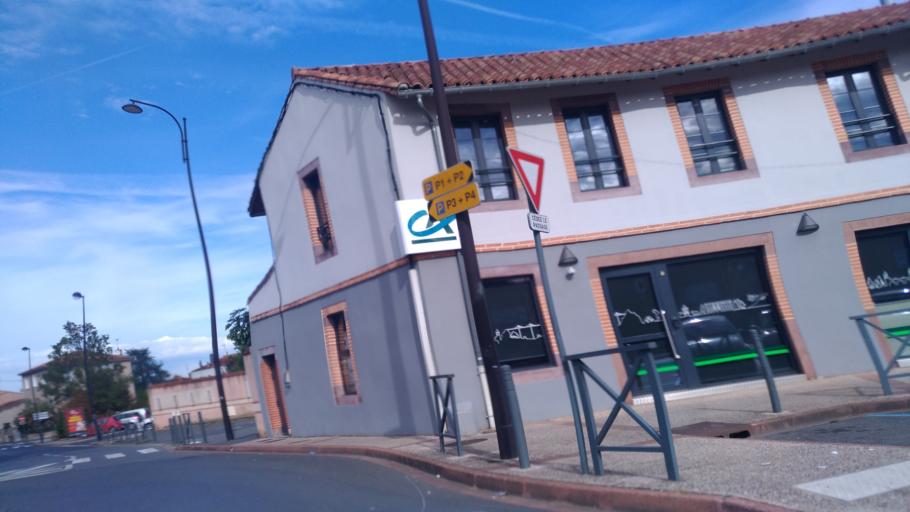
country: FR
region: Midi-Pyrenees
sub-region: Departement du Tarn
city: Albi
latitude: 43.9223
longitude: 2.1629
